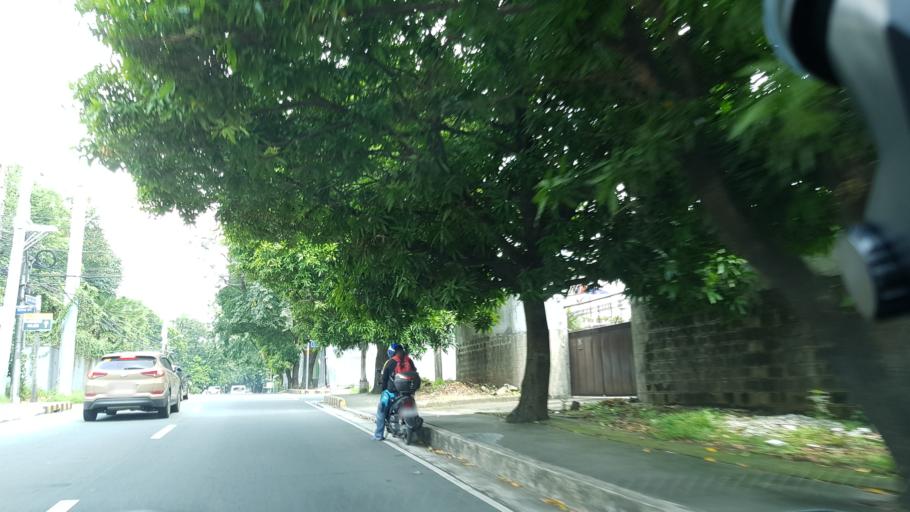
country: PH
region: Metro Manila
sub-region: San Juan
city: San Juan
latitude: 14.6211
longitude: 121.0333
